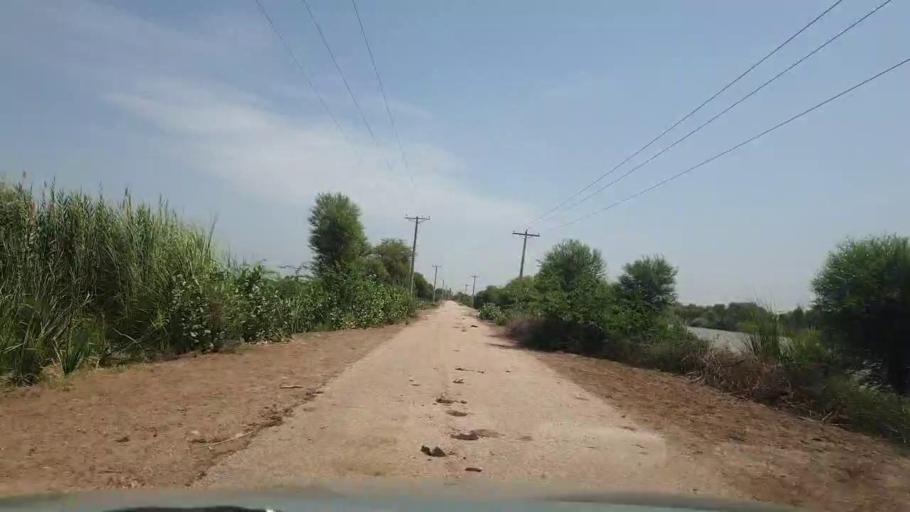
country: PK
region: Sindh
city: Bozdar
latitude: 27.1161
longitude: 68.9897
